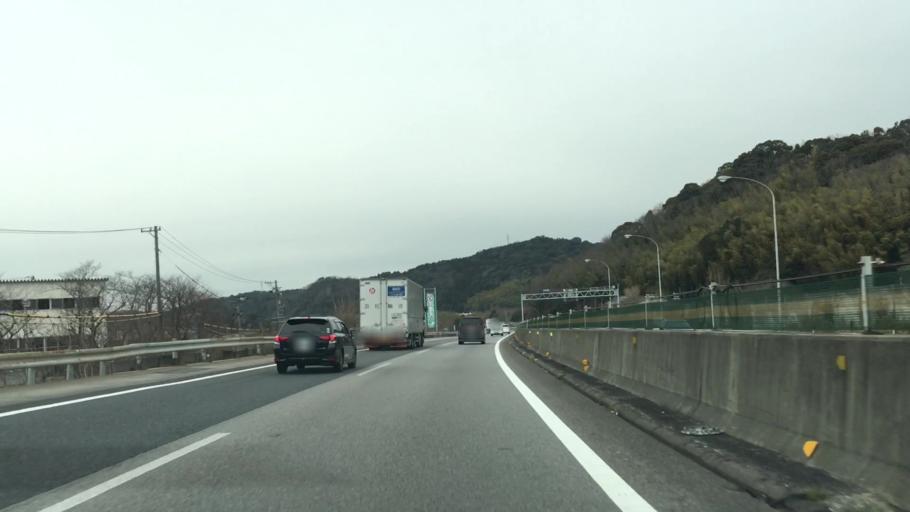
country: JP
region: Aichi
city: Okazaki
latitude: 34.9273
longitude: 137.2233
